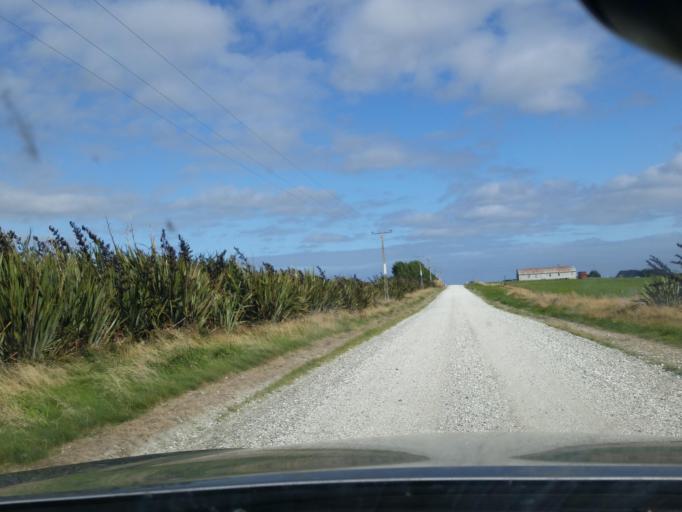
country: NZ
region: Southland
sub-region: Invercargill City
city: Invercargill
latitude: -46.4468
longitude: 168.5062
